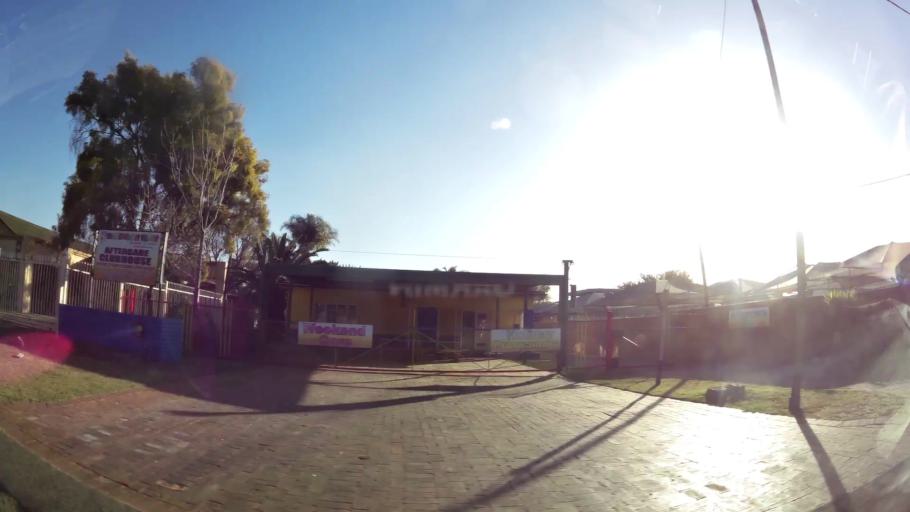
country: ZA
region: Gauteng
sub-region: City of Tshwane Metropolitan Municipality
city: Pretoria
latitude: -25.7184
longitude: 28.2099
